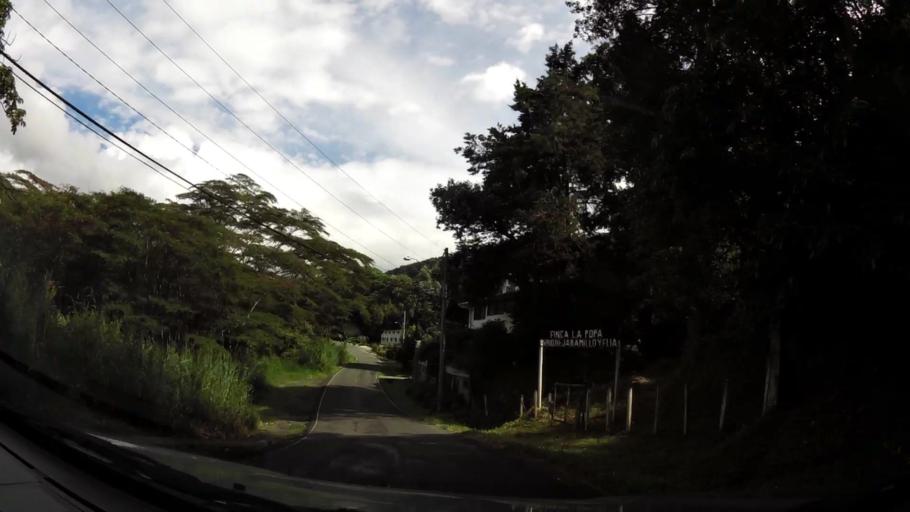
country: PA
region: Chiriqui
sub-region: Distrito Boquete
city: Boquete
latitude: 8.7832
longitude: -82.4293
